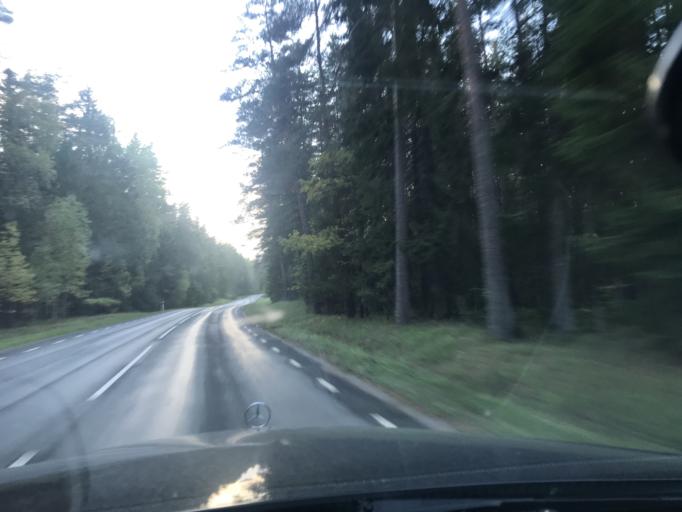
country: EE
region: Vorumaa
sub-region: Antsla vald
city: Vana-Antsla
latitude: 57.8799
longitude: 26.7612
